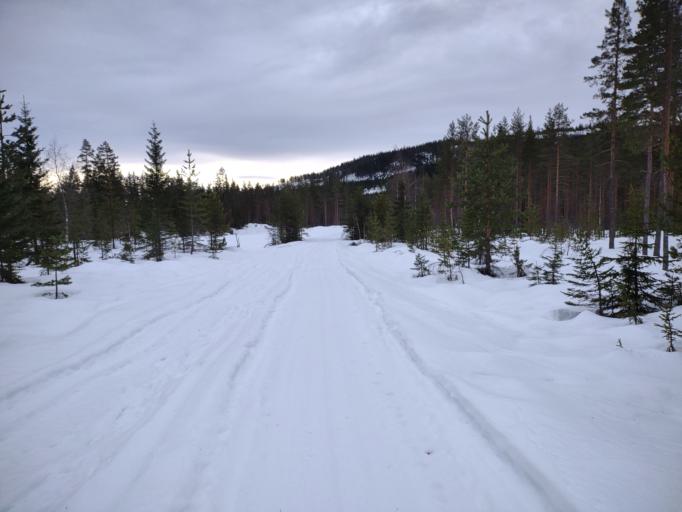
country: NO
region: Buskerud
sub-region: Flesberg
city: Lampeland
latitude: 59.7269
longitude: 9.5368
